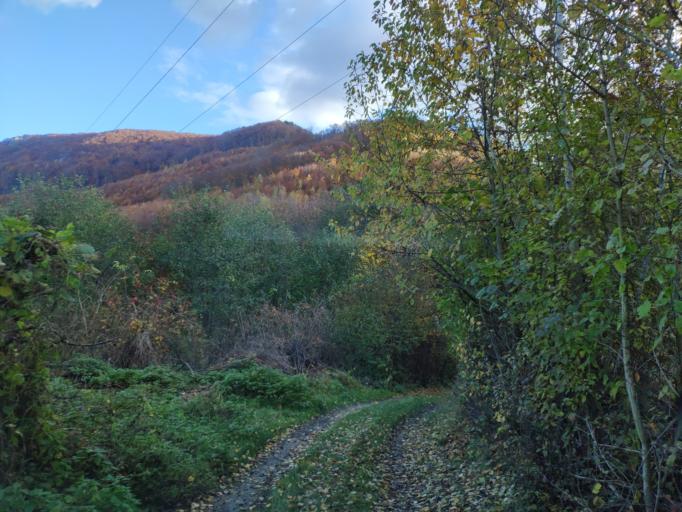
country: SK
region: Presovsky
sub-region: Okres Presov
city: Presov
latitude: 48.8517
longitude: 21.1654
